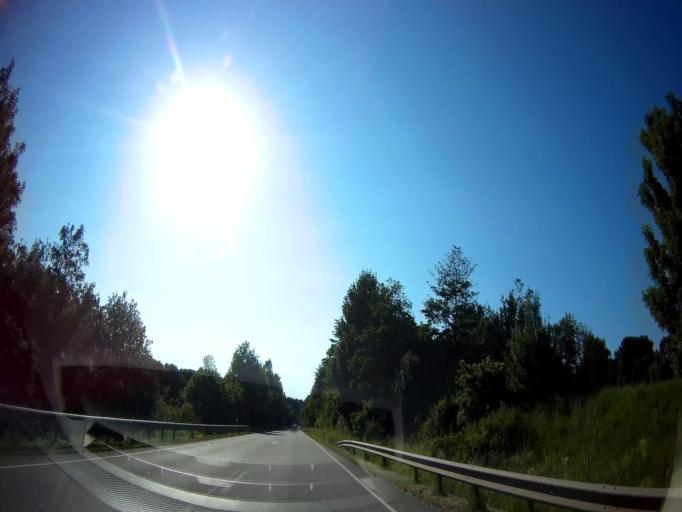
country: DE
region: Bavaria
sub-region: Lower Bavaria
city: Eggenfelden
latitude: 48.4192
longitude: 12.7660
